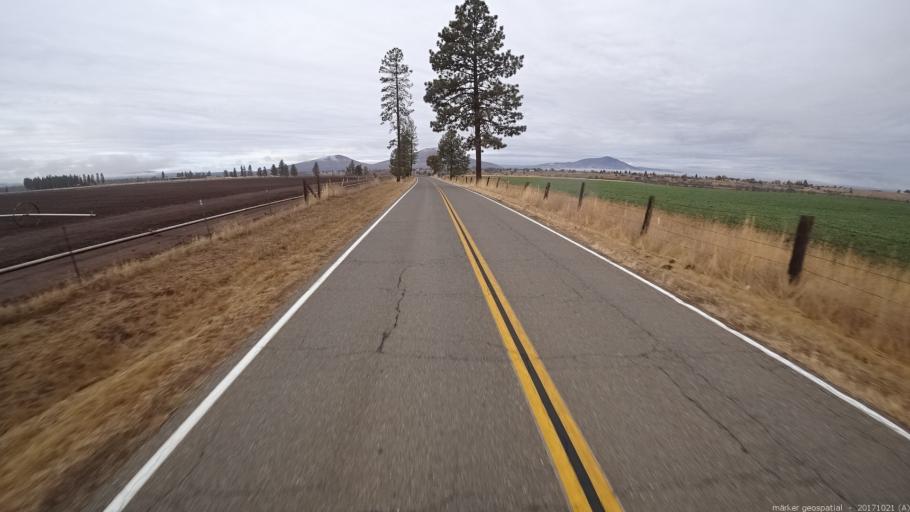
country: US
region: California
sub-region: Shasta County
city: Burney
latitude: 41.0255
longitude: -121.4000
